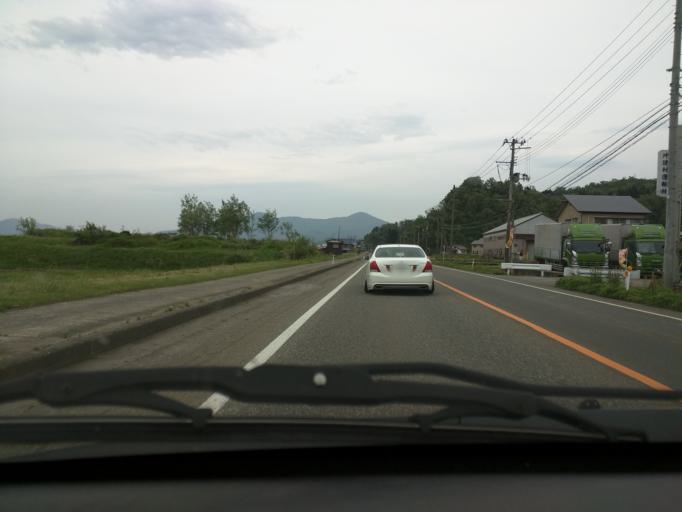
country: JP
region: Niigata
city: Muikamachi
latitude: 37.1948
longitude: 138.9478
